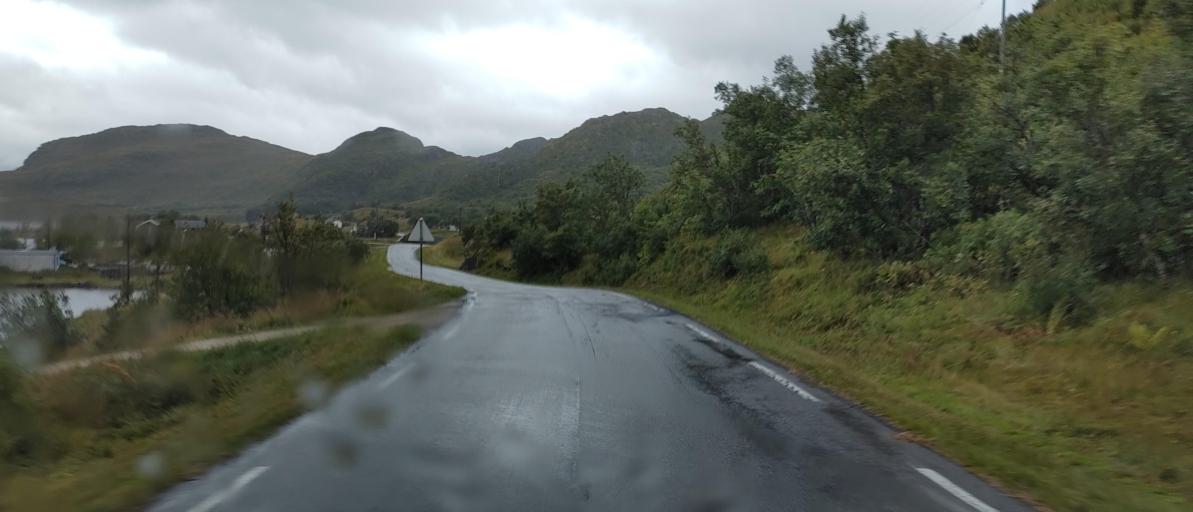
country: NO
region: Nordland
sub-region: Vestvagoy
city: Evjen
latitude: 68.2729
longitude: 13.7364
